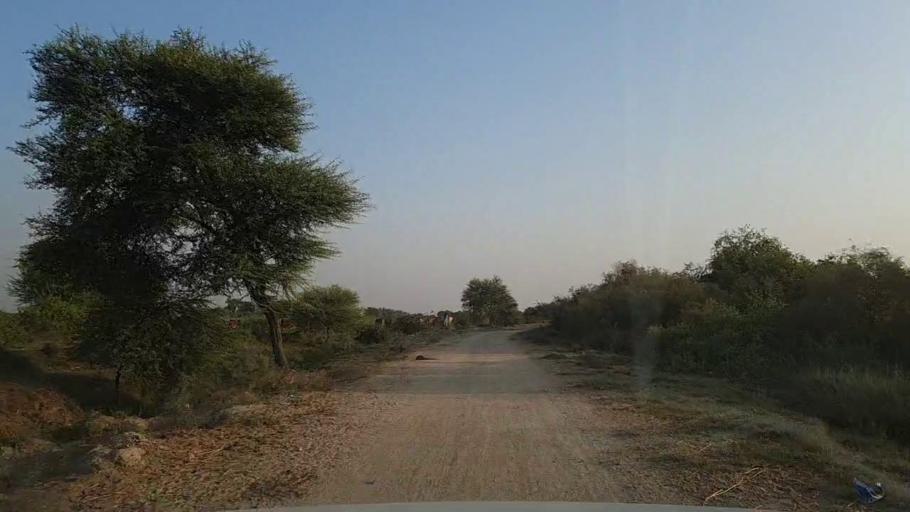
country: PK
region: Sindh
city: Daro Mehar
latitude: 24.7435
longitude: 68.1840
